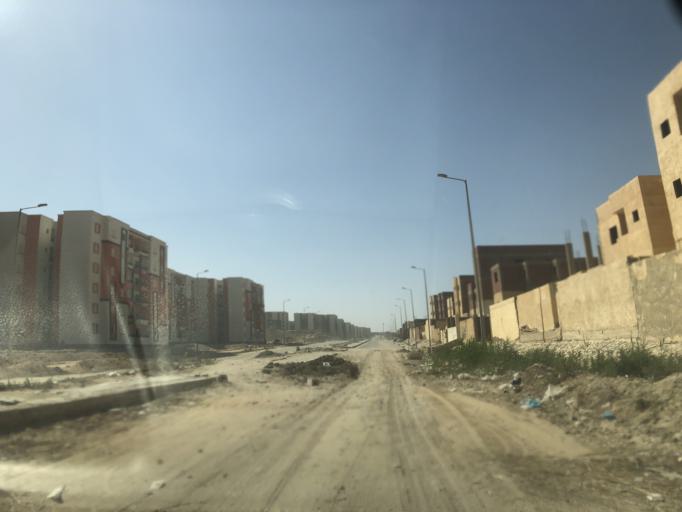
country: EG
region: Al Jizah
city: Madinat Sittah Uktubar
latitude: 29.9270
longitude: 30.9950
